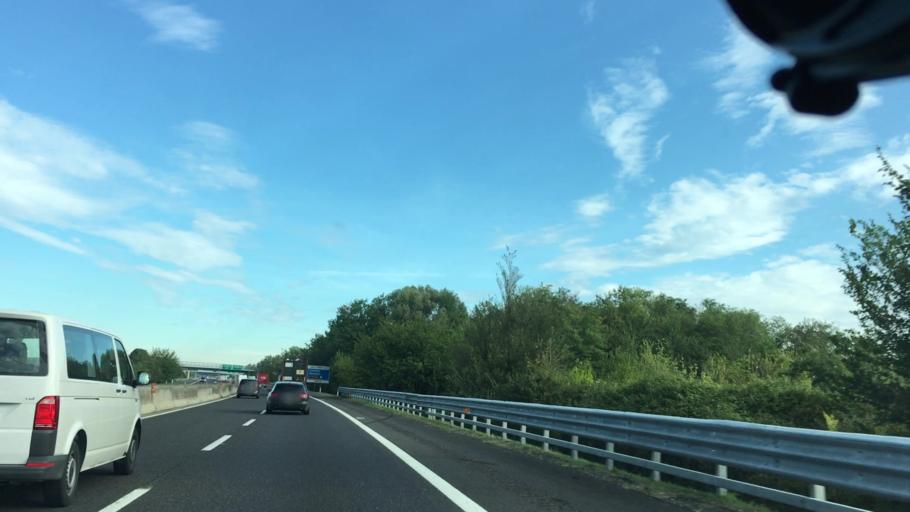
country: IT
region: Emilia-Romagna
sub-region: Provincia di Ferrara
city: Porotto-Cassama
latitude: 44.8587
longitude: 11.5699
